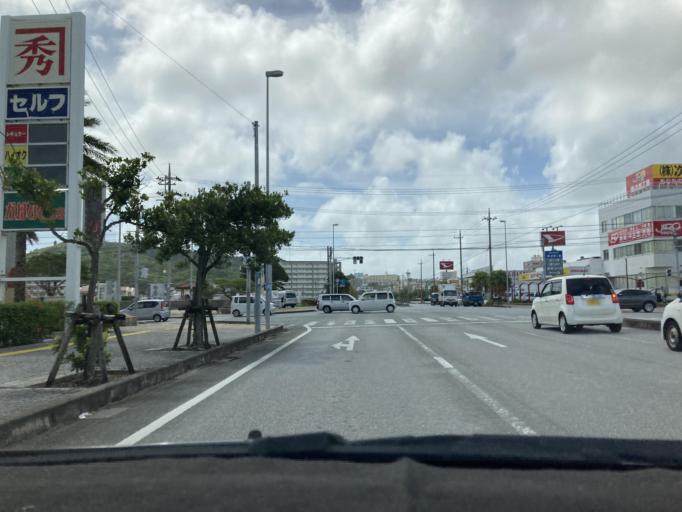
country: JP
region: Okinawa
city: Ginowan
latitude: 26.2061
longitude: 127.7624
